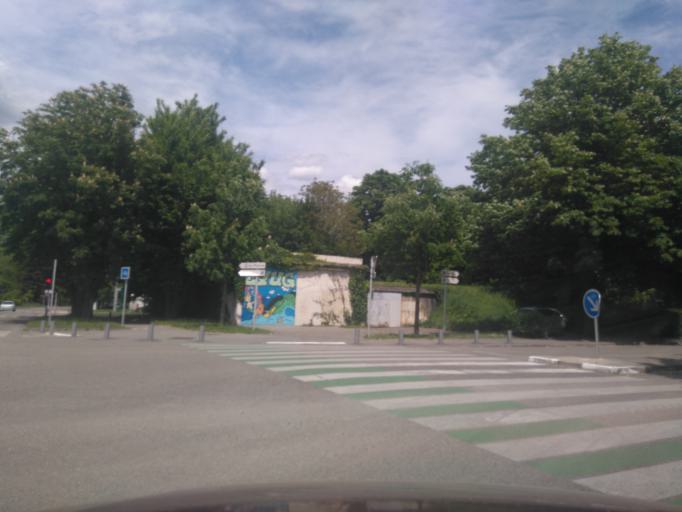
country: FR
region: Rhone-Alpes
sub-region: Departement de l'Isere
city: Corenc
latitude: 45.1913
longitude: 5.7593
